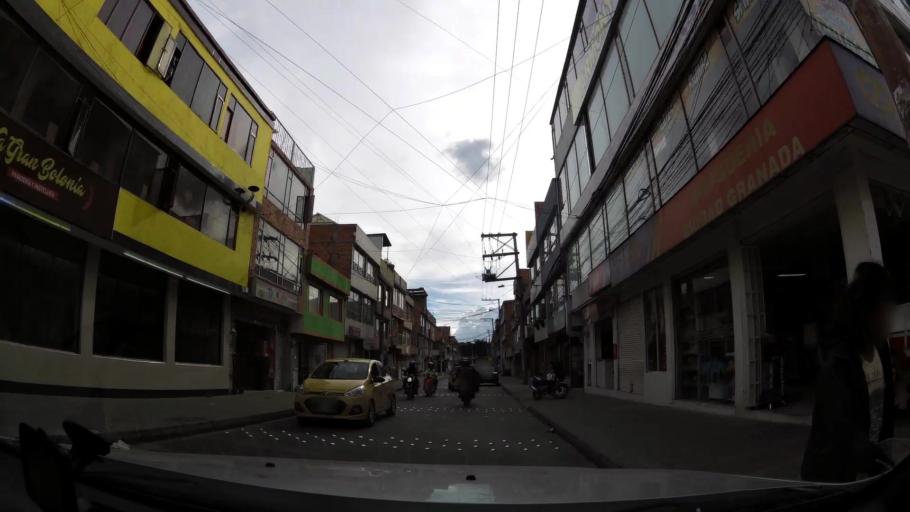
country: CO
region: Cundinamarca
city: Soacha
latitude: 4.6417
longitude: -74.1708
